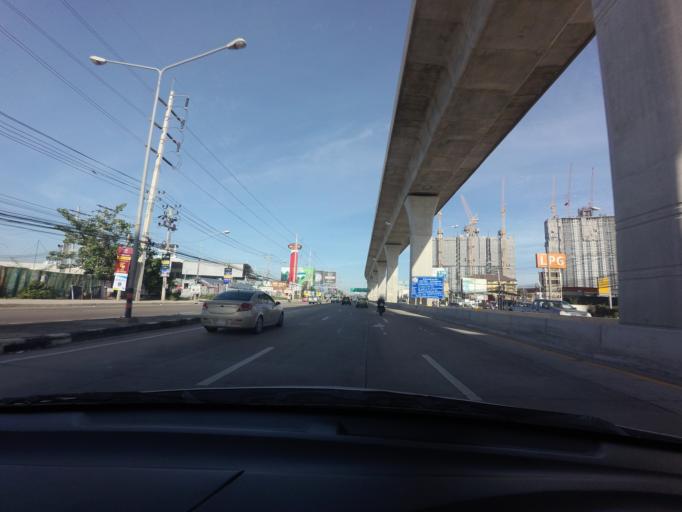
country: TH
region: Nonthaburi
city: Bang Bua Thong
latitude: 13.8744
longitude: 100.4171
